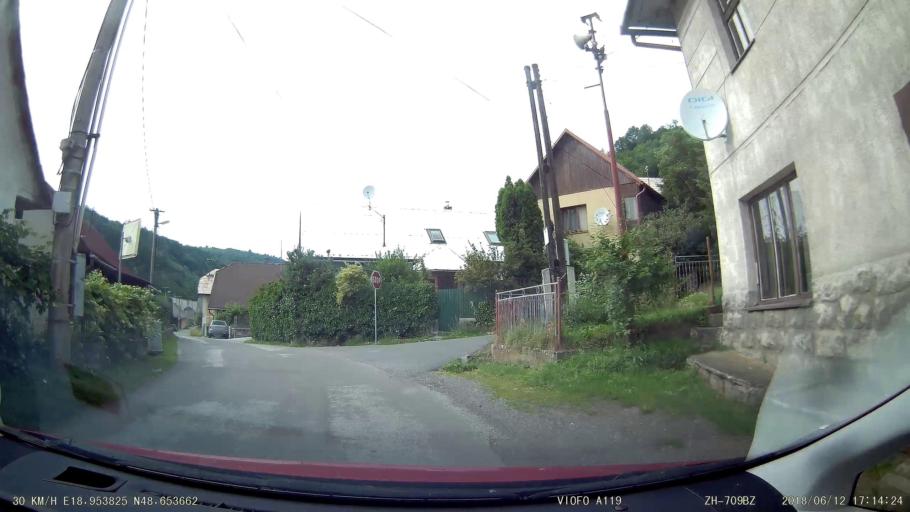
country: SK
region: Banskobystricky
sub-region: Okres Ziar nad Hronom
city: Kremnica
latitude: 48.6539
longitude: 18.9539
